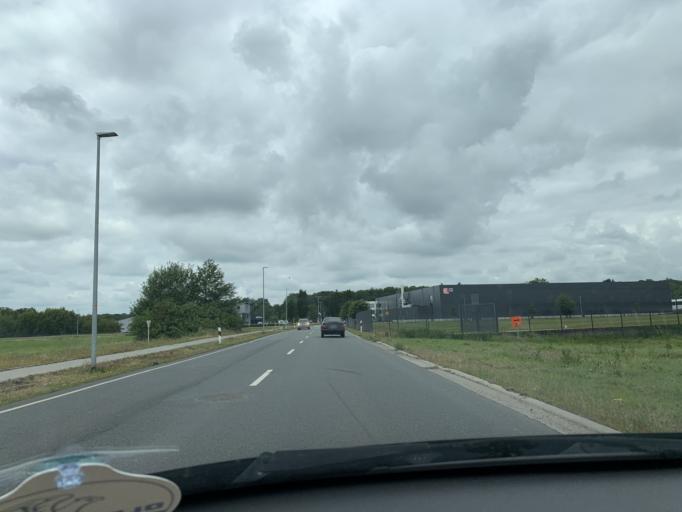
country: DE
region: Lower Saxony
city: Varel
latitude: 53.3960
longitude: 8.1175
